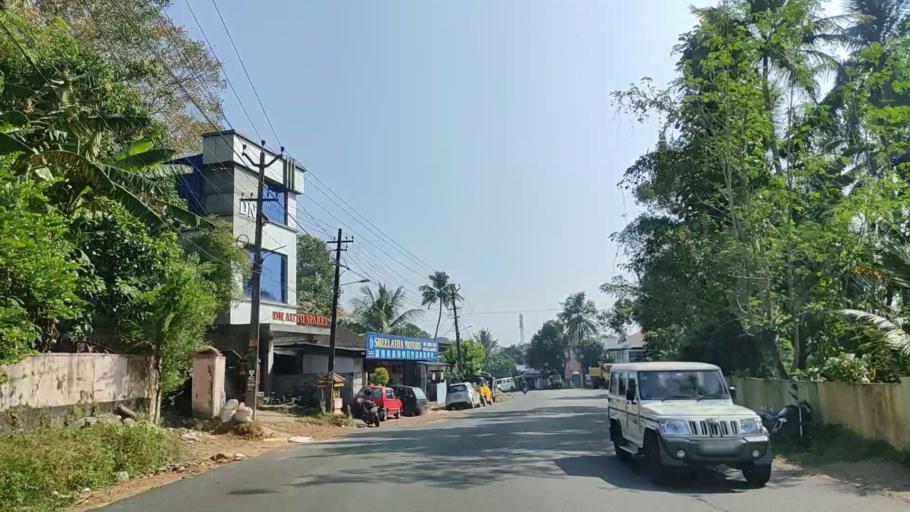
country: IN
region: Kerala
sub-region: Kollam
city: Punalur
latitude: 8.9290
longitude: 76.9270
